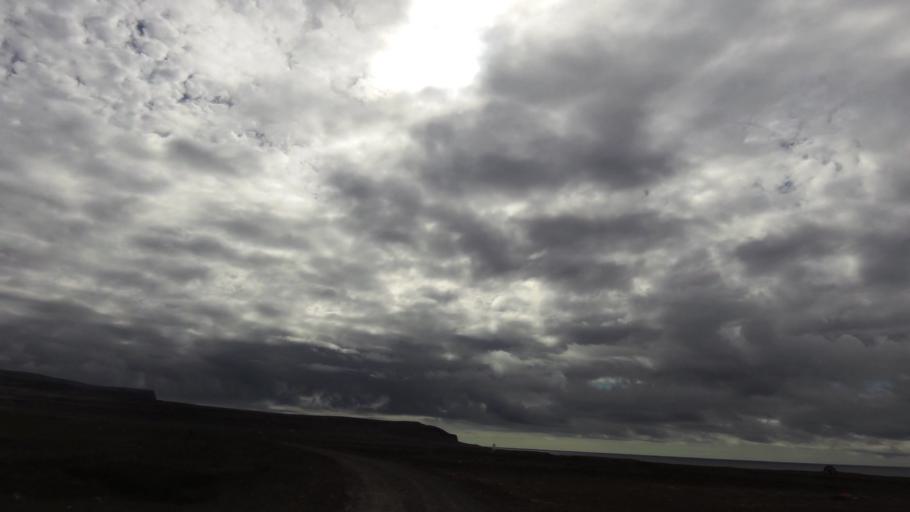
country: IS
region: West
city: Olafsvik
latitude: 65.6144
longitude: -24.3264
